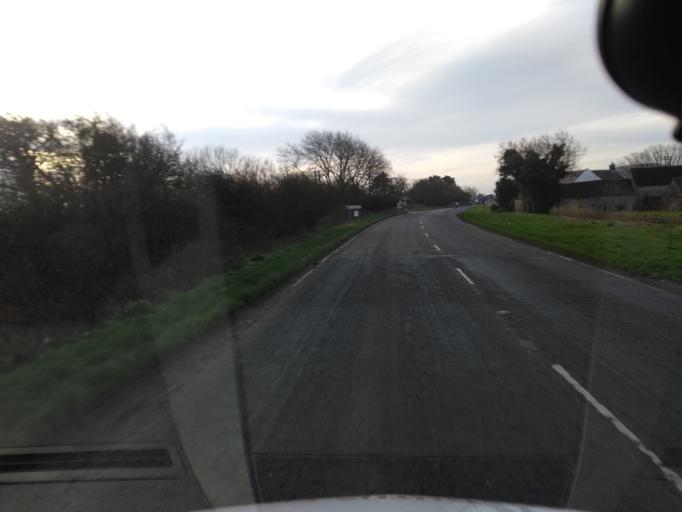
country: GB
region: England
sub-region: North Somerset
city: Bleadon
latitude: 51.2781
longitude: -2.9331
